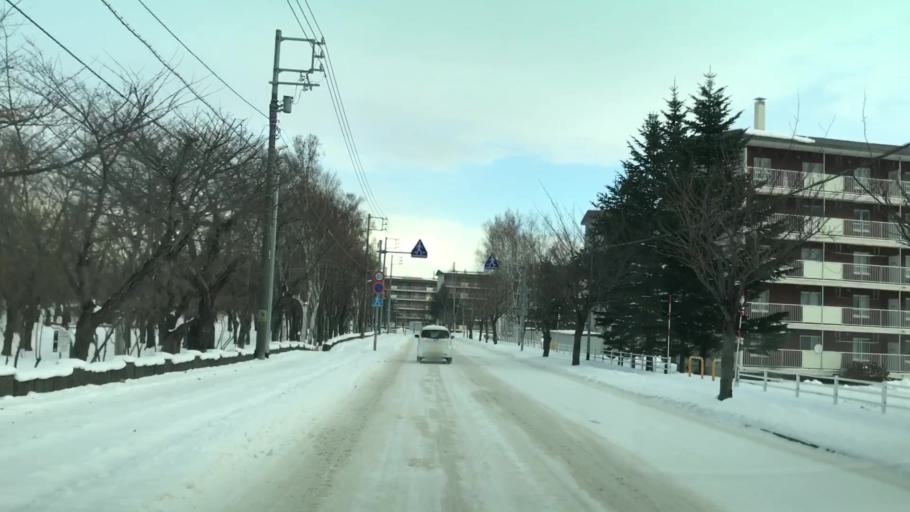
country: JP
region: Hokkaido
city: Sapporo
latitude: 43.0853
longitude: 141.3033
